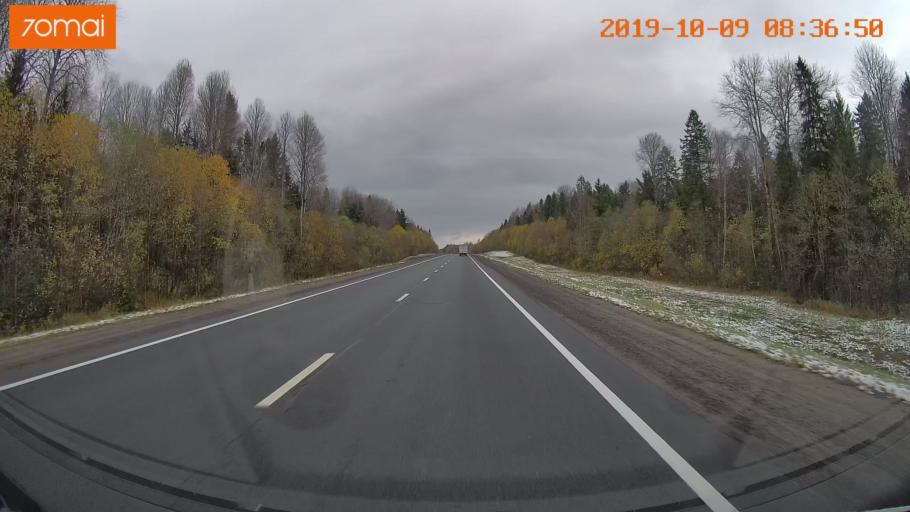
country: RU
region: Vologda
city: Gryazovets
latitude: 58.9323
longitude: 40.1758
